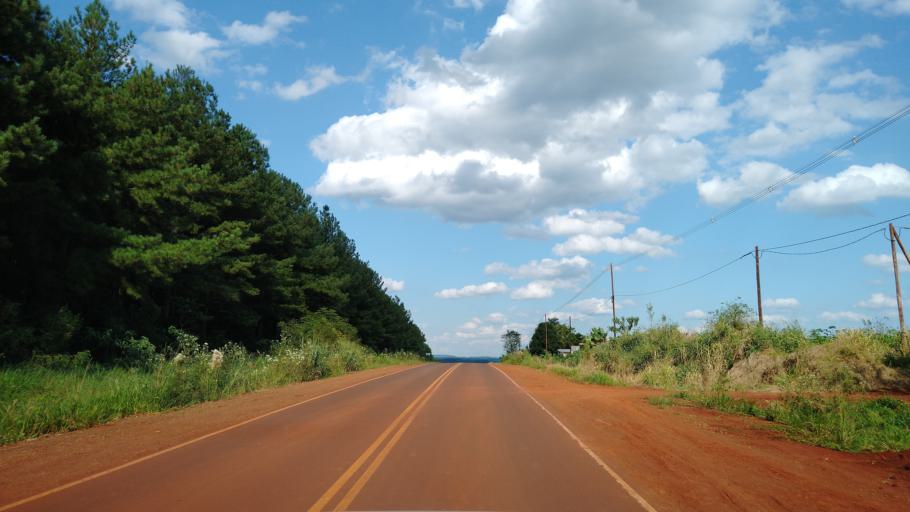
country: AR
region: Misiones
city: Puerto Piray
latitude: -26.4767
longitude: -54.6791
